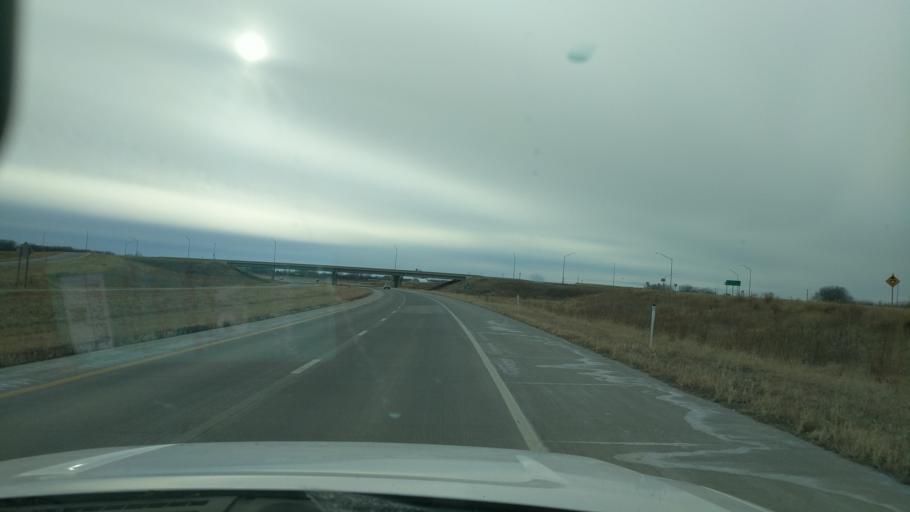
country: US
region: Kansas
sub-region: Riley County
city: Manhattan
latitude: 39.1564
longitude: -96.6410
